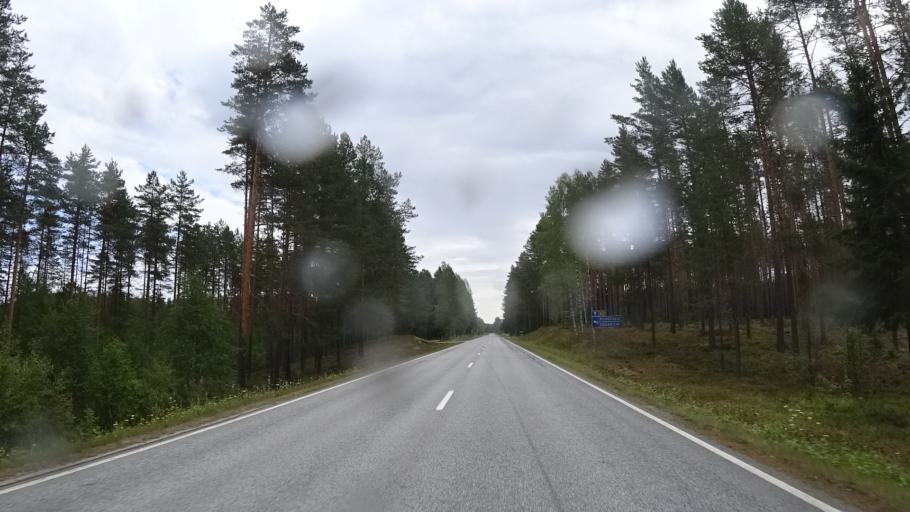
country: FI
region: North Karelia
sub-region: Keski-Karjala
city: Kesaelahti
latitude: 62.1105
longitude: 29.7324
